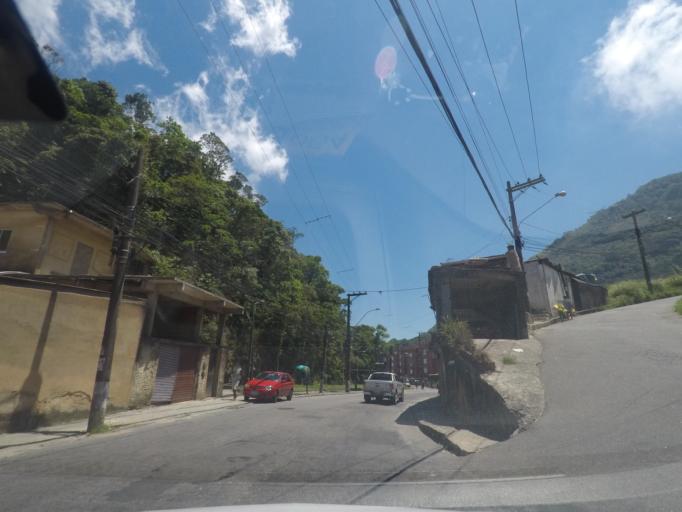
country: BR
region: Rio de Janeiro
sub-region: Petropolis
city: Petropolis
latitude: -22.5311
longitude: -43.1726
